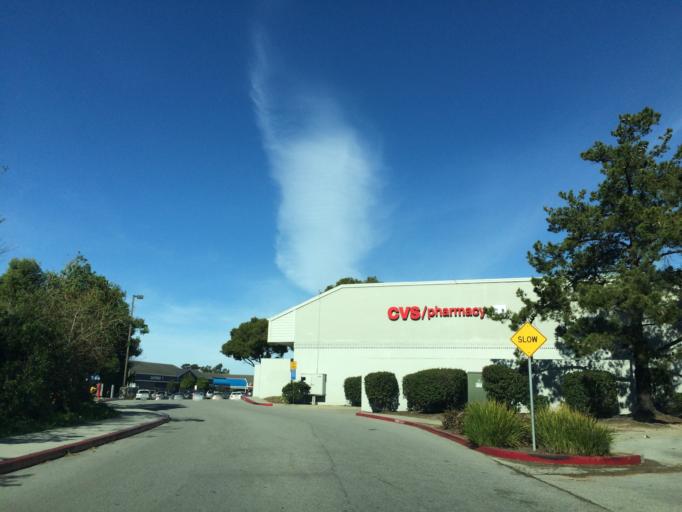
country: US
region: California
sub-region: San Mateo County
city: Half Moon Bay
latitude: 37.4684
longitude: -122.4347
